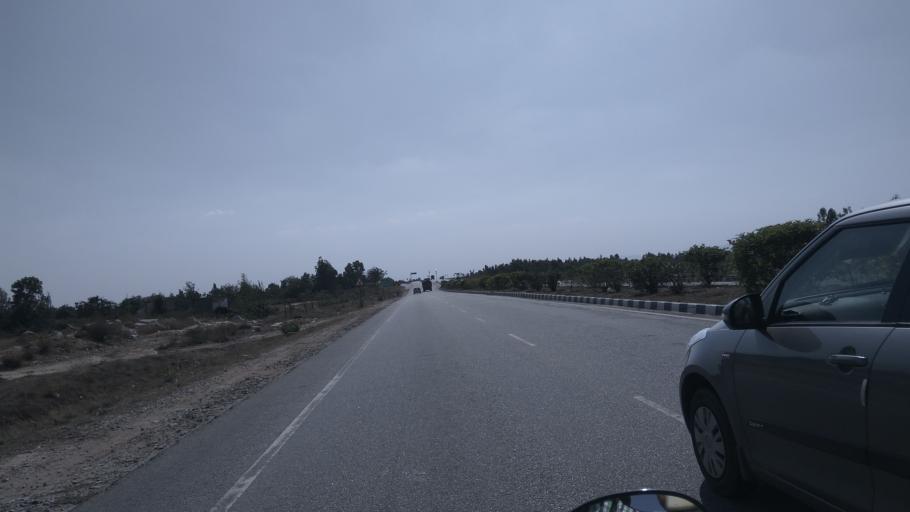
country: IN
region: Karnataka
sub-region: Kolar
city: Mulbagal
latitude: 13.1530
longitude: 78.3050
